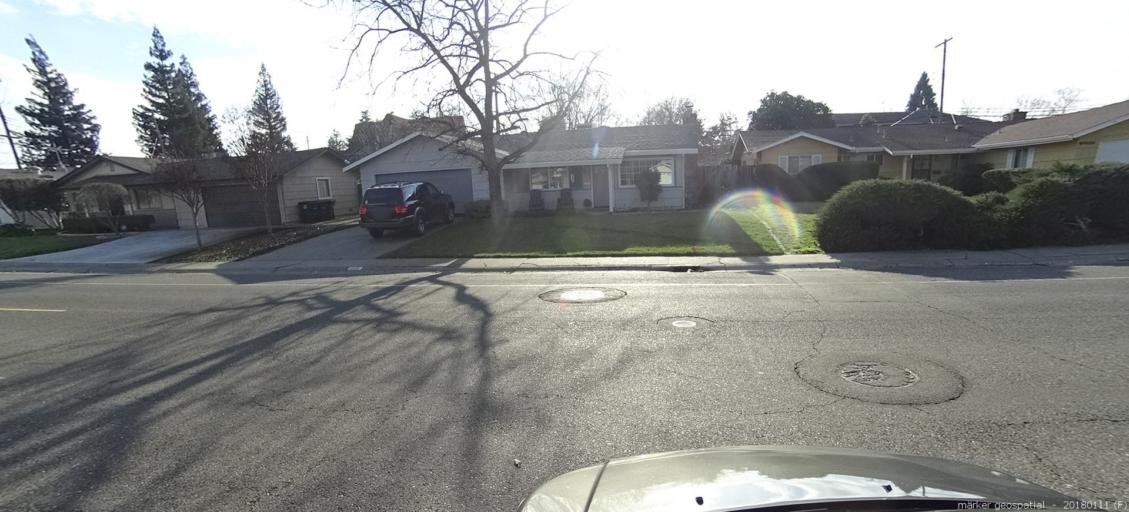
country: US
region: California
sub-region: Sacramento County
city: Rancho Cordova
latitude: 38.6035
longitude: -121.3000
